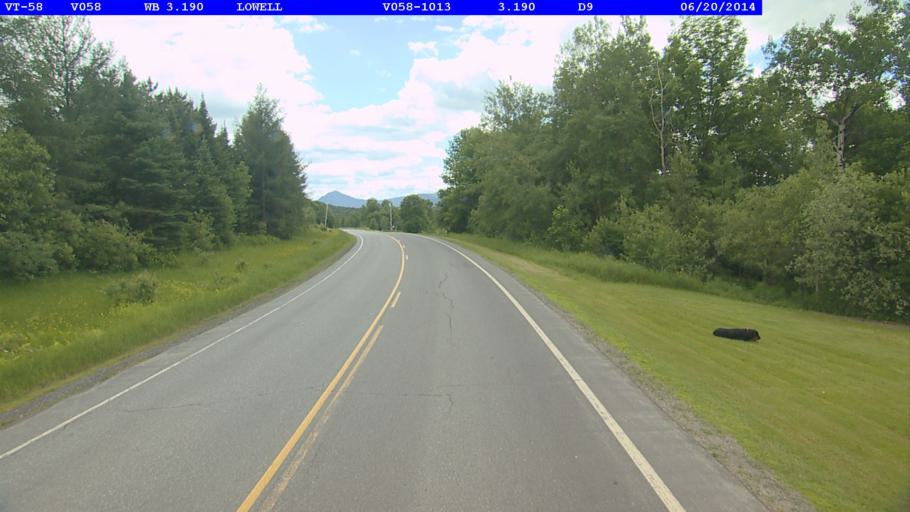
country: US
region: Vermont
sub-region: Orleans County
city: Newport
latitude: 44.8156
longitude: -72.3953
